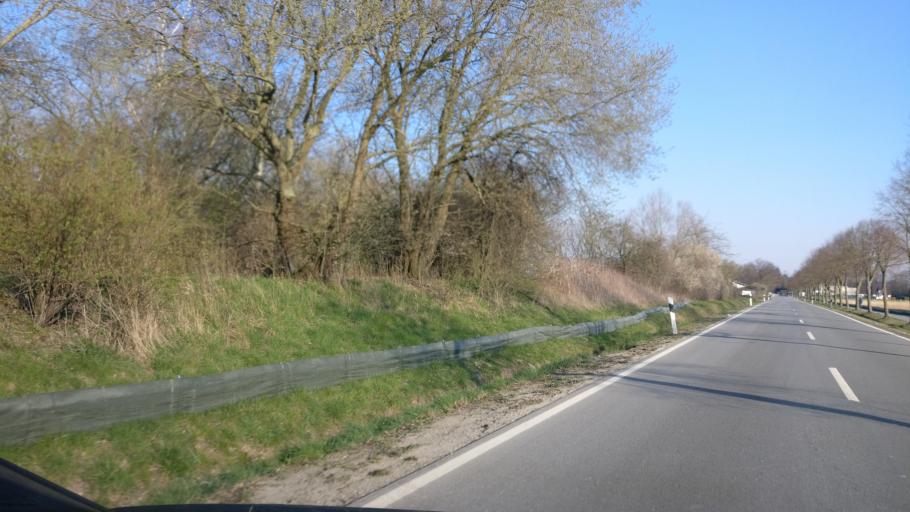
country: DE
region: North Rhine-Westphalia
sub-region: Regierungsbezirk Detmold
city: Lage
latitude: 52.0001
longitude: 8.7711
